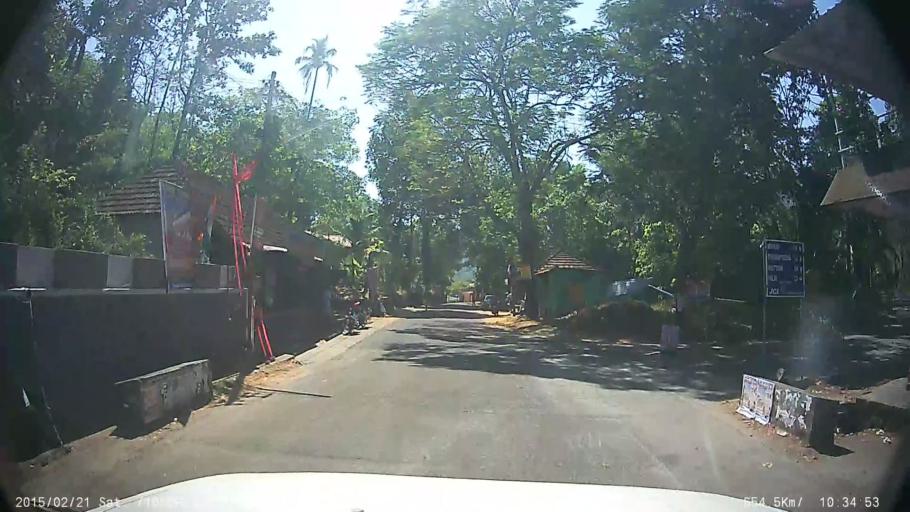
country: IN
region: Kerala
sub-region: Kottayam
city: Lalam
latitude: 9.8258
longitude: 76.7207
